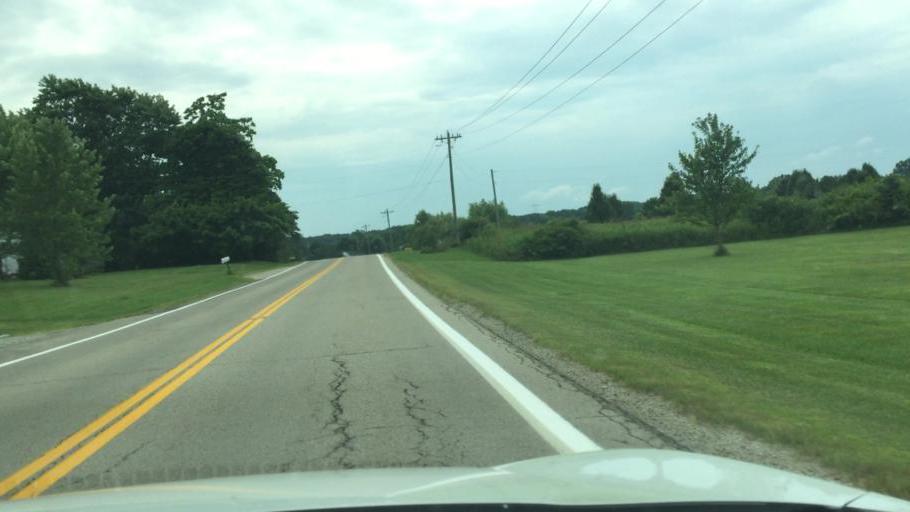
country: US
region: Ohio
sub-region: Champaign County
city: Mechanicsburg
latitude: 40.0983
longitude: -83.5766
